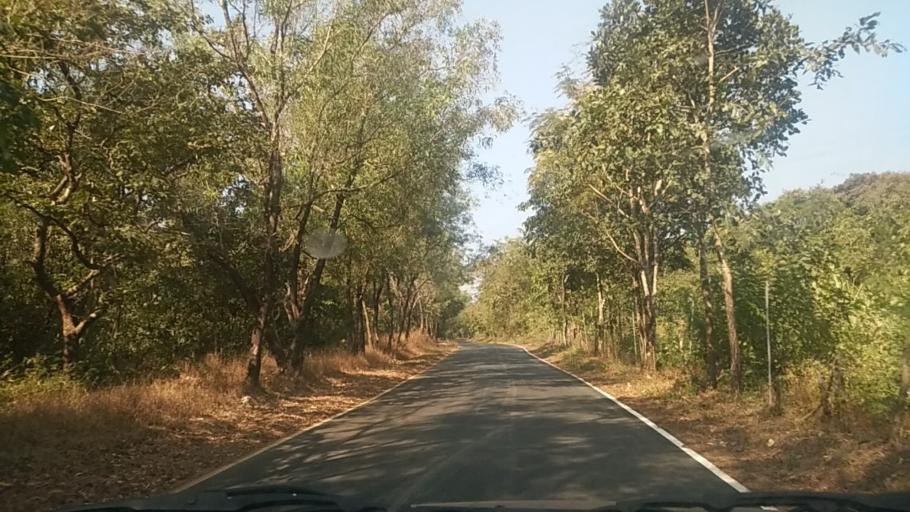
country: IN
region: Goa
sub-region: South Goa
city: Sanguem
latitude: 15.2014
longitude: 74.2252
